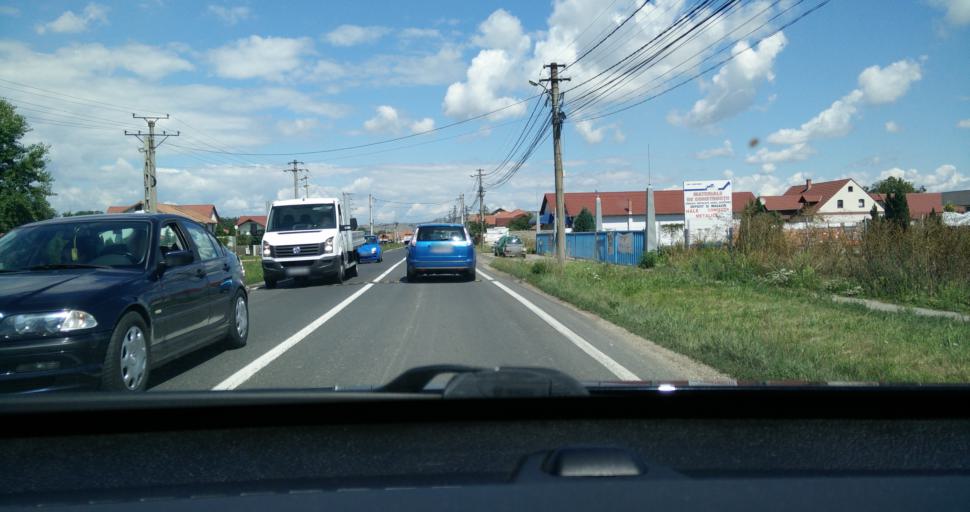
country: RO
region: Alba
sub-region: Municipiul Sebes
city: Petresti
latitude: 45.9393
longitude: 23.5628
